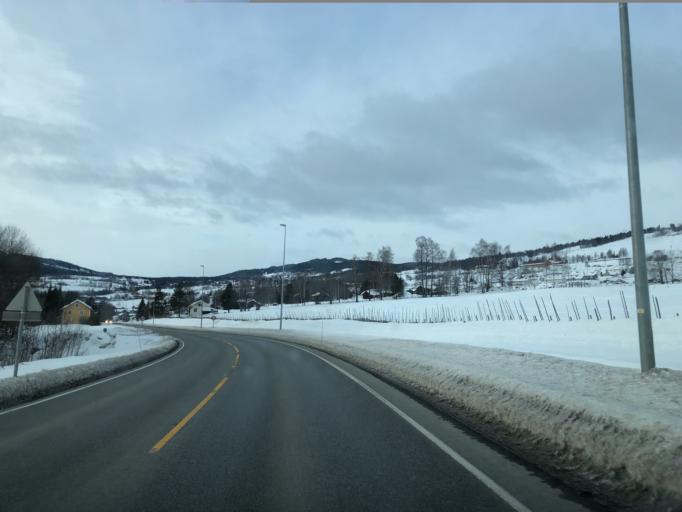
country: NO
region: Oppland
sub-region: Gausdal
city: Segalstad bru
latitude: 61.2090
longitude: 10.2978
